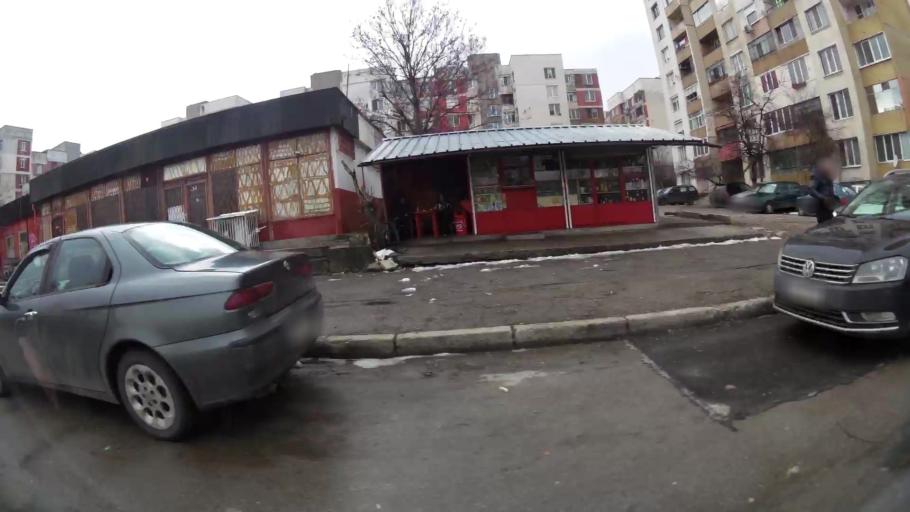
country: BG
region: Sofiya
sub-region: Obshtina Bozhurishte
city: Bozhurishte
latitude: 42.7247
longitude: 23.2509
